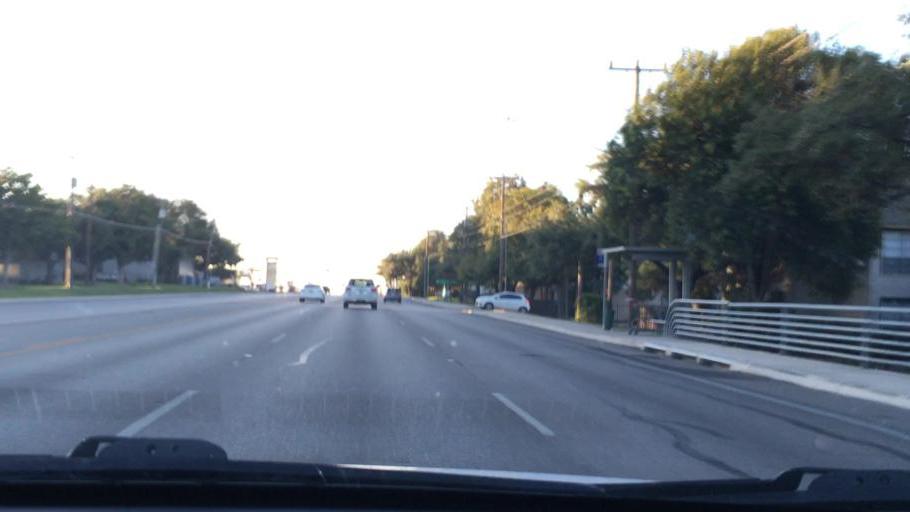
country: US
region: Texas
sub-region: Bexar County
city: Castle Hills
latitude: 29.5469
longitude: -98.5304
